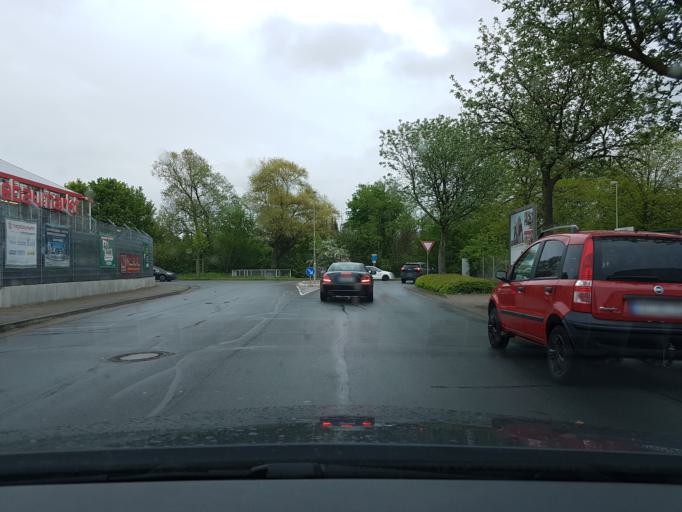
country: DE
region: Lower Saxony
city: Hameln
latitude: 52.0920
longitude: 9.3746
